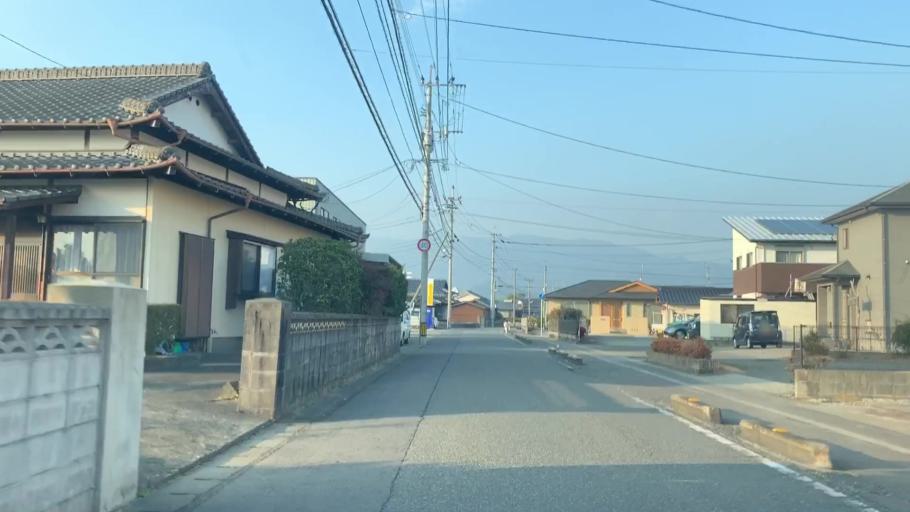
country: JP
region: Saga Prefecture
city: Saga-shi
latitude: 33.2764
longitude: 130.2268
